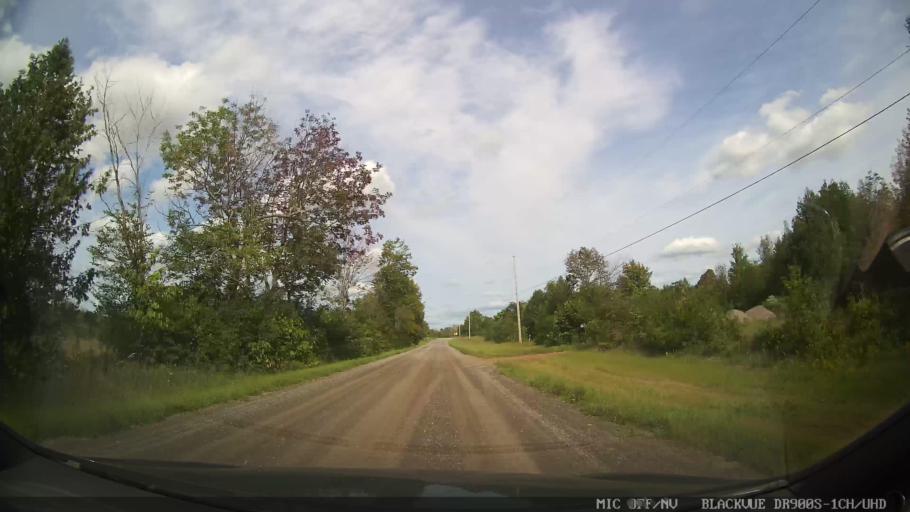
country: CA
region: Ontario
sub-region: Lanark County
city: Smiths Falls
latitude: 44.9254
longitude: -75.9368
